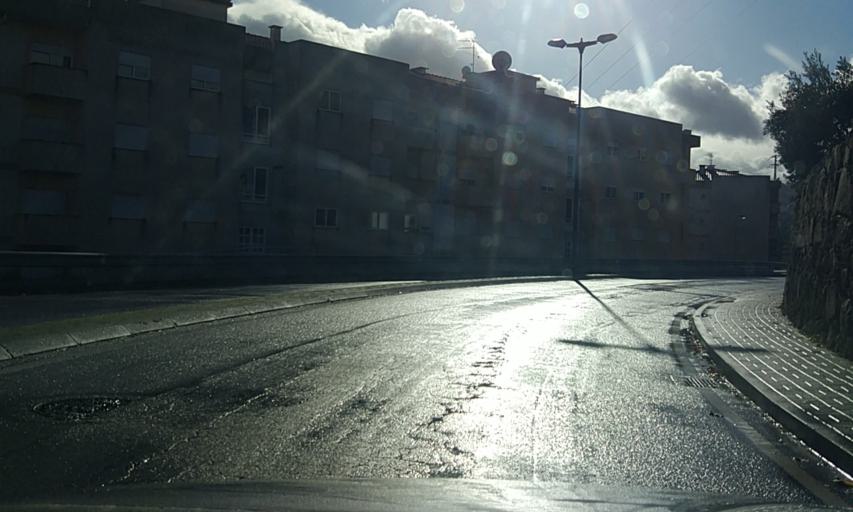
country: PT
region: Viseu
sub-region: Lamego
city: Lamego
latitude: 41.1025
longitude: -7.7955
